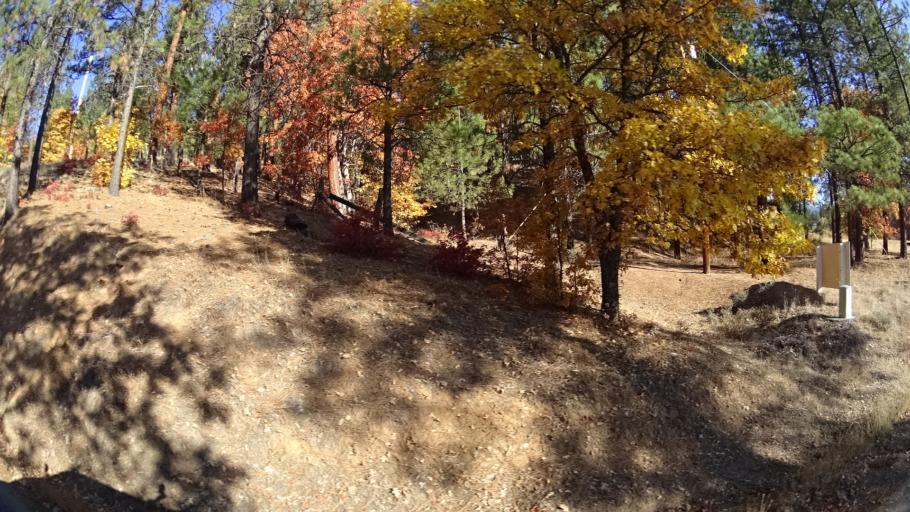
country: US
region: California
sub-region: Siskiyou County
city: Yreka
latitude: 41.6416
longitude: -122.9969
